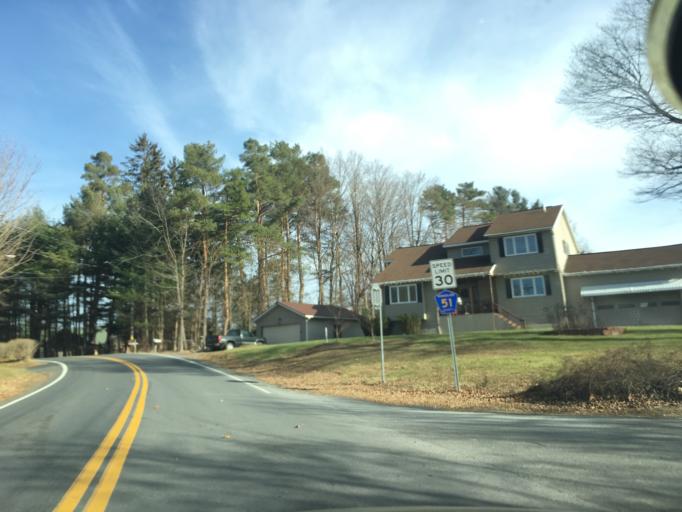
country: US
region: New York
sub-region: Rensselaer County
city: Averill Park
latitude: 42.6149
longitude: -73.5689
